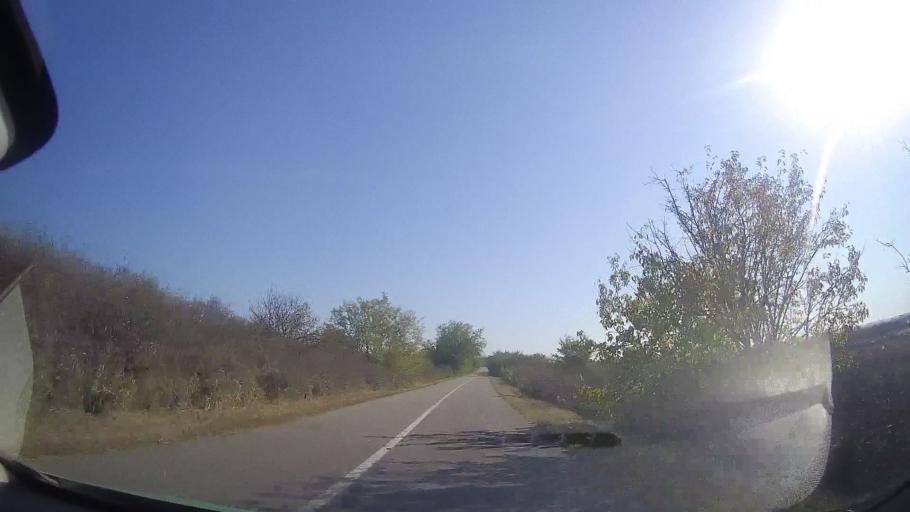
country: RO
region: Timis
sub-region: Comuna Ghizela
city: Ghizela
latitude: 45.8269
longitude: 21.7322
